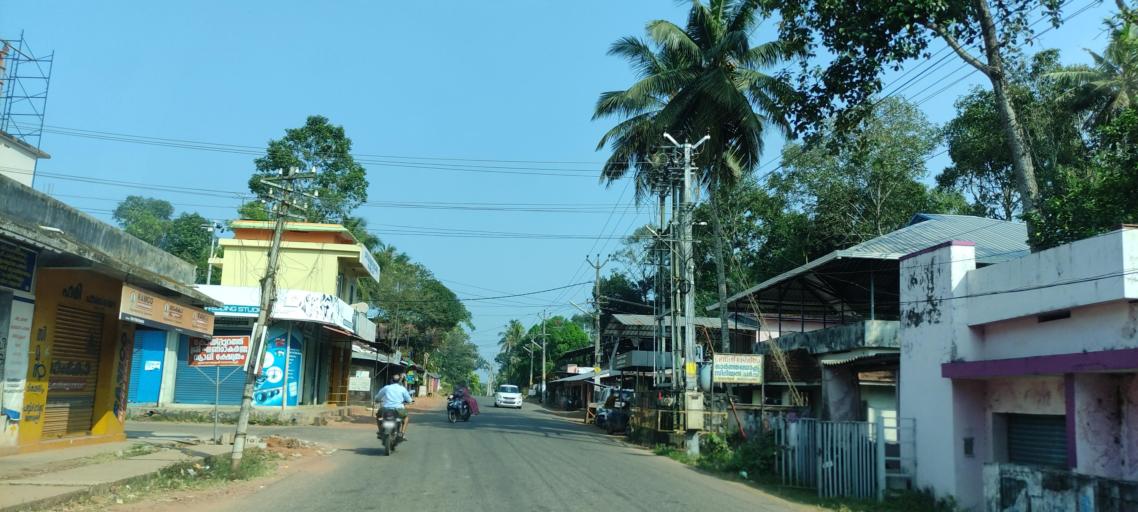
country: IN
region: Kerala
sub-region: Kollam
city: Panmana
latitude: 9.0410
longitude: 76.5959
